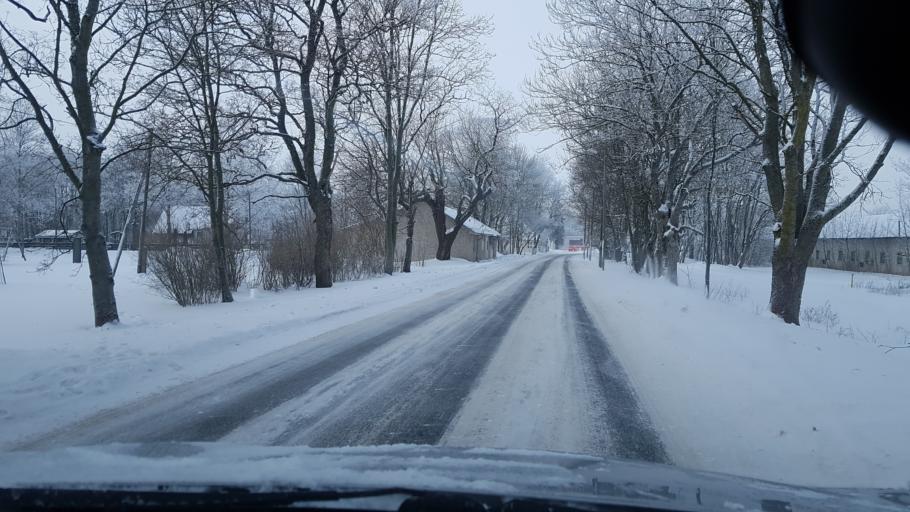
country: EE
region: Harju
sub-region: Keila linn
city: Keila
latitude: 59.3224
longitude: 24.4542
